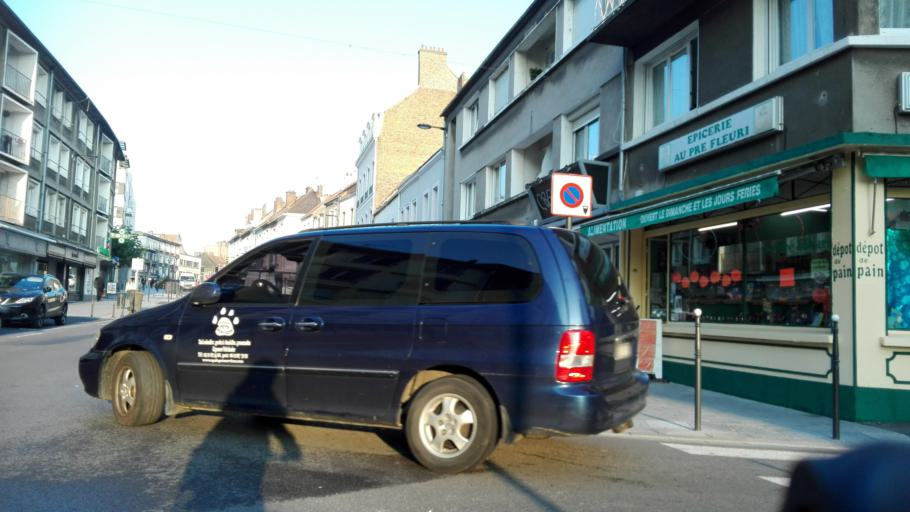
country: FR
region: Nord-Pas-de-Calais
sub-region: Departement du Pas-de-Calais
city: Boulogne-sur-Mer
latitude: 50.7218
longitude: 1.6098
